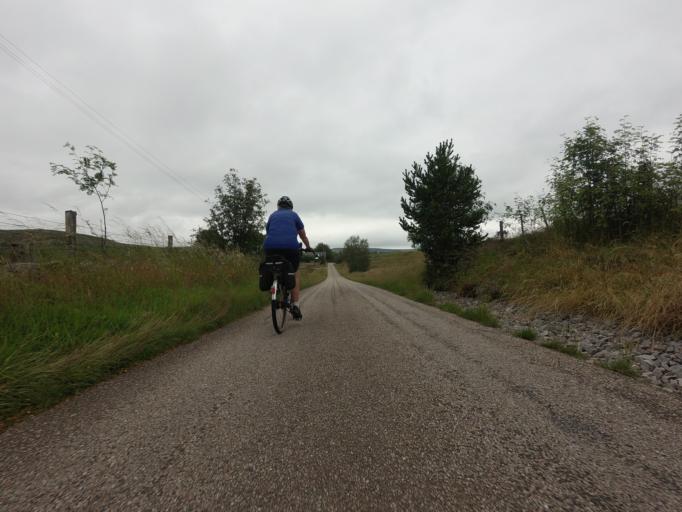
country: GB
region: Scotland
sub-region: Highland
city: Alness
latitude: 58.0065
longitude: -4.4051
